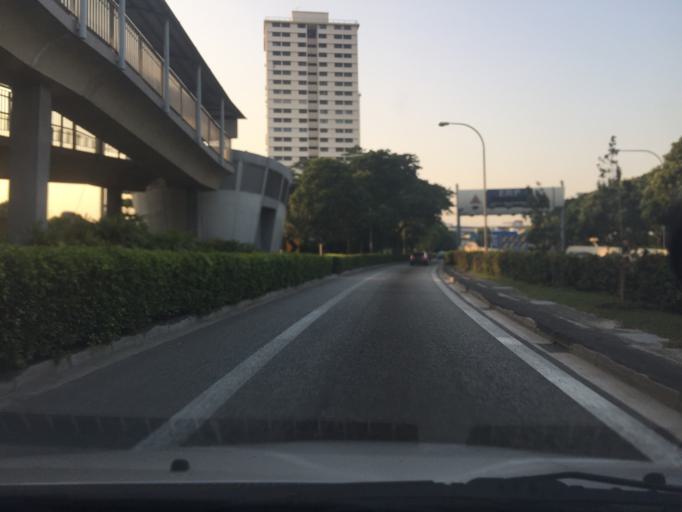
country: SG
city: Singapore
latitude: 1.3166
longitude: 103.8743
